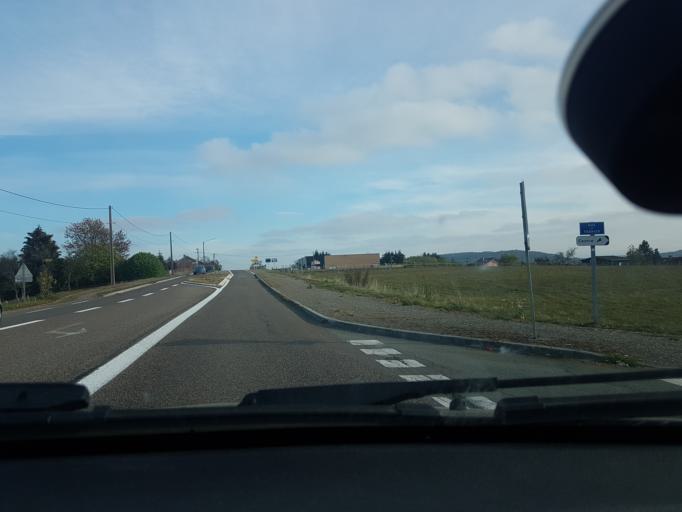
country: FR
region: Franche-Comte
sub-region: Departement de la Haute-Saone
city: Chalonvillars
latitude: 47.6459
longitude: 6.7797
